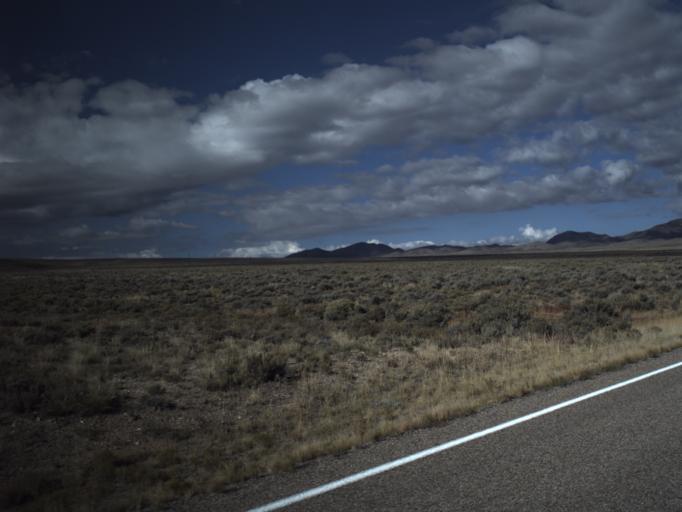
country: US
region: Utah
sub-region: Beaver County
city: Milford
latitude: 38.4307
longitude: -113.1272
